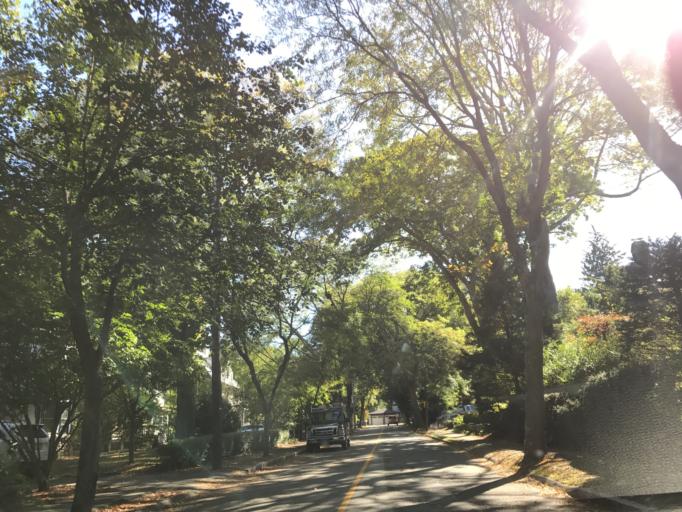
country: US
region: Massachusetts
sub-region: Norfolk County
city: Brookline
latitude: 42.3275
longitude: -71.1604
